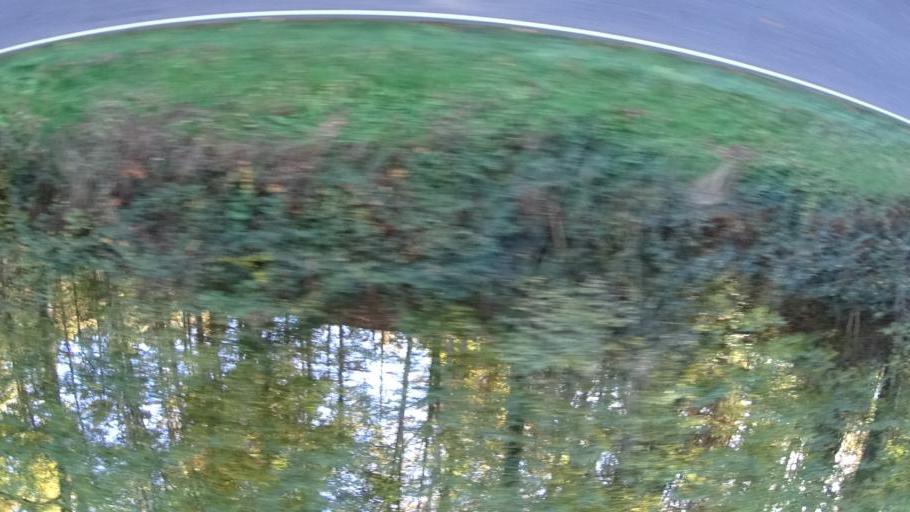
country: DE
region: Baden-Wuerttemberg
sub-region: Karlsruhe Region
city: Konigsbach-Stein
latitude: 48.9545
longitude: 8.5633
